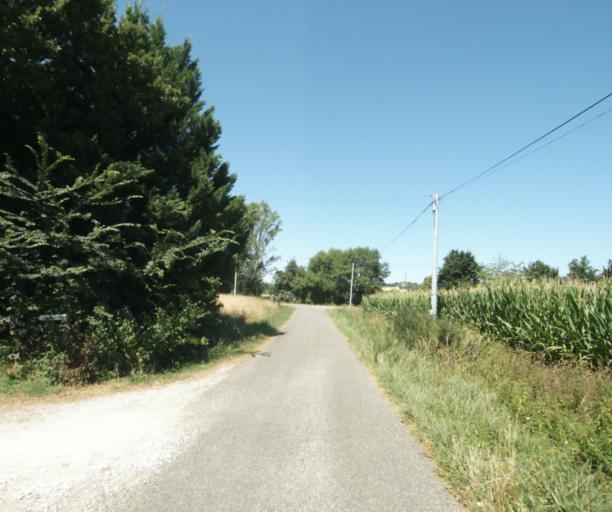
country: FR
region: Midi-Pyrenees
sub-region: Departement de la Haute-Garonne
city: Revel
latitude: 43.4891
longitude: 1.9580
